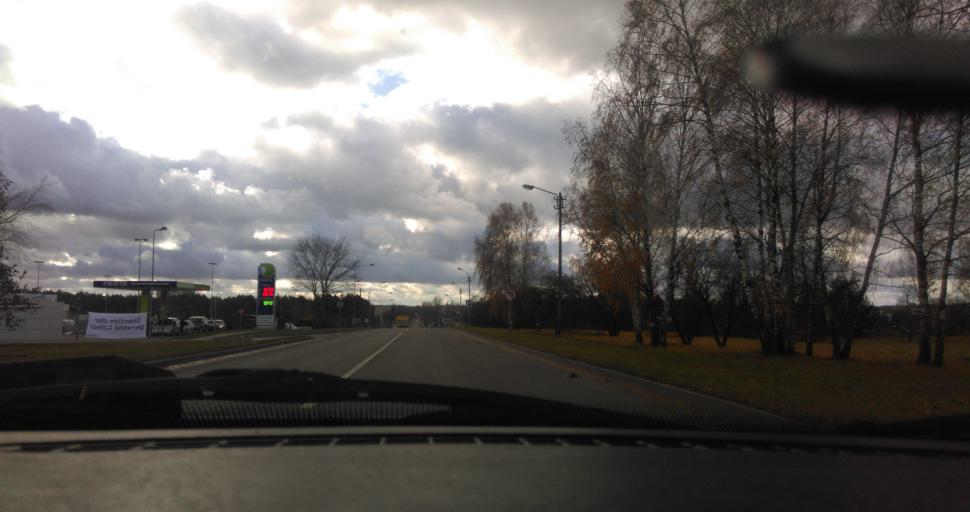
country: LT
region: Utenos apskritis
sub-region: Utena
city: Utena
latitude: 55.5058
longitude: 25.6255
